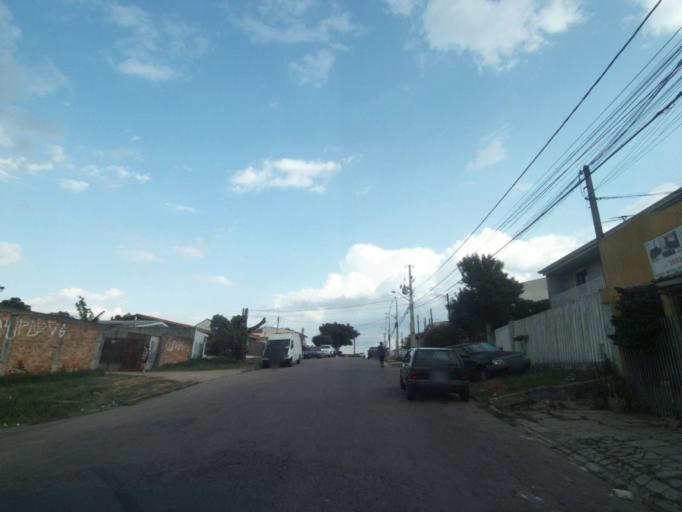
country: BR
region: Parana
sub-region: Sao Jose Dos Pinhais
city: Sao Jose dos Pinhais
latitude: -25.5348
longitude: -49.2773
